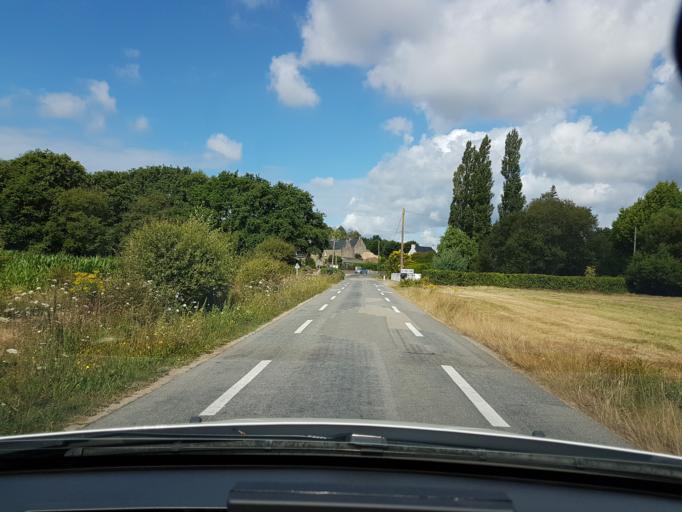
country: FR
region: Brittany
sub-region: Departement du Morbihan
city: Sainte-Helene
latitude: 47.7159
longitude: -3.1969
